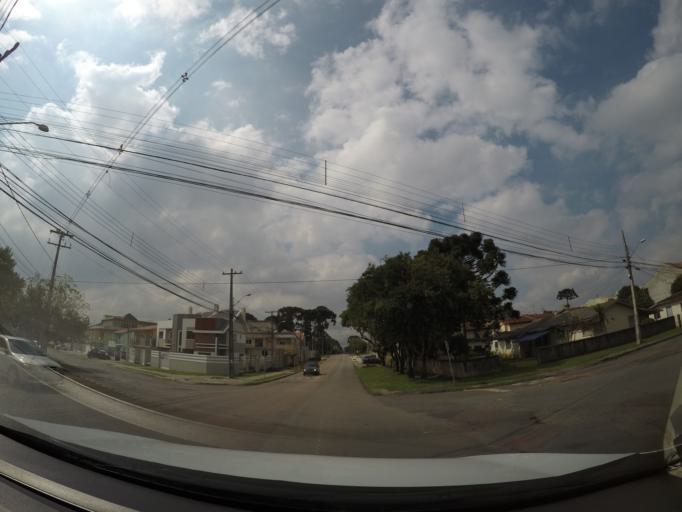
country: BR
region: Parana
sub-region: Sao Jose Dos Pinhais
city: Sao Jose dos Pinhais
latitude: -25.5009
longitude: -49.2476
